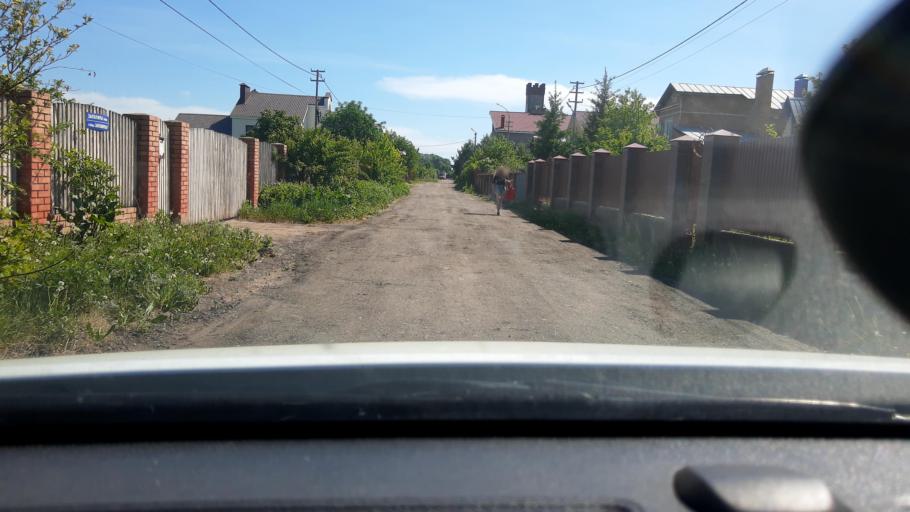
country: RU
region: Bashkortostan
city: Avdon
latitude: 54.5047
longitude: 55.8205
